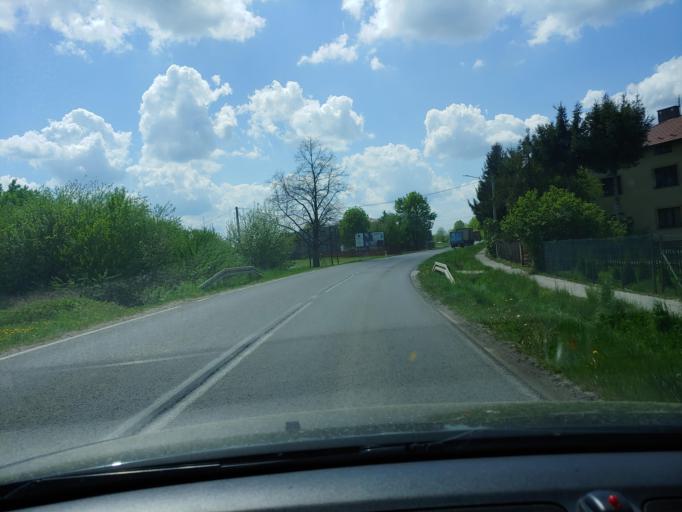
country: PL
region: Subcarpathian Voivodeship
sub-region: Powiat mielecki
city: Radomysl Wielki
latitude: 50.1898
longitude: 21.2674
